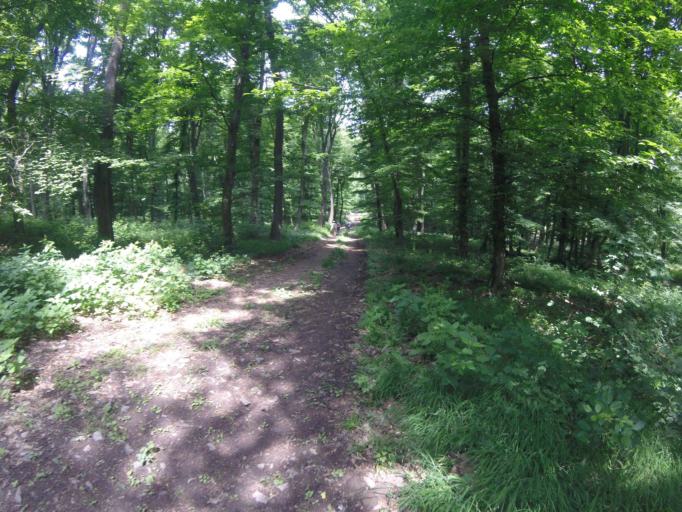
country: HU
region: Zala
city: Cserszegtomaj
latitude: 46.9067
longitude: 17.1932
